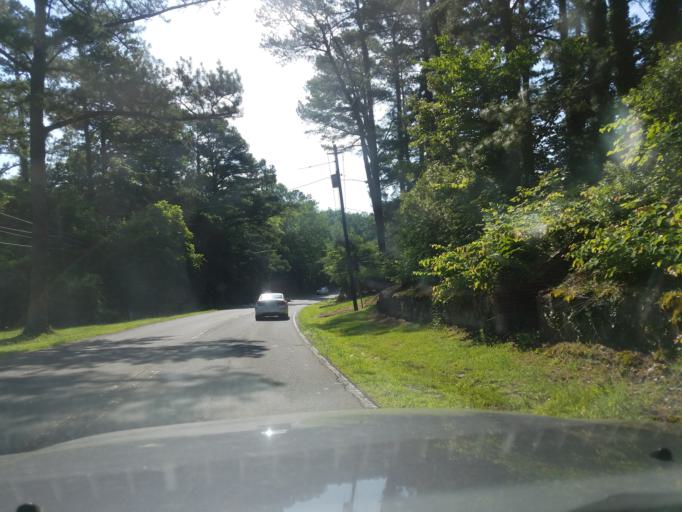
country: US
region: North Carolina
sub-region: Granville County
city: Oxford
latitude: 36.3179
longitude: -78.5784
